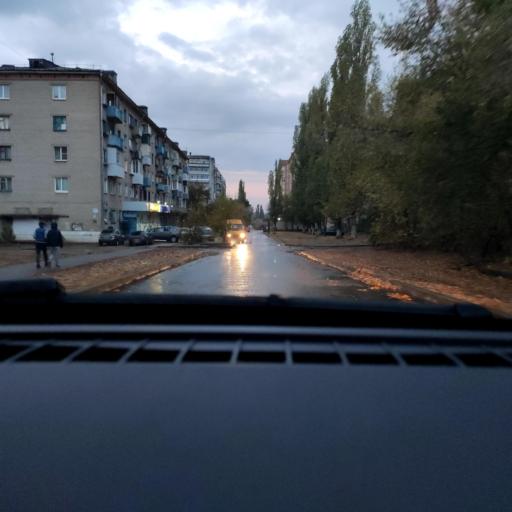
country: RU
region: Voronezj
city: Maslovka
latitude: 51.6113
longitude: 39.2323
